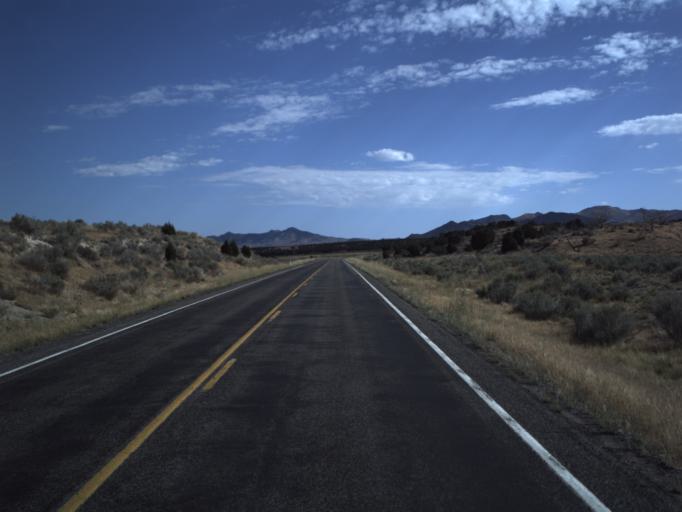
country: US
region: Utah
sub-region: Juab County
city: Mona
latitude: 39.7534
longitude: -112.1822
